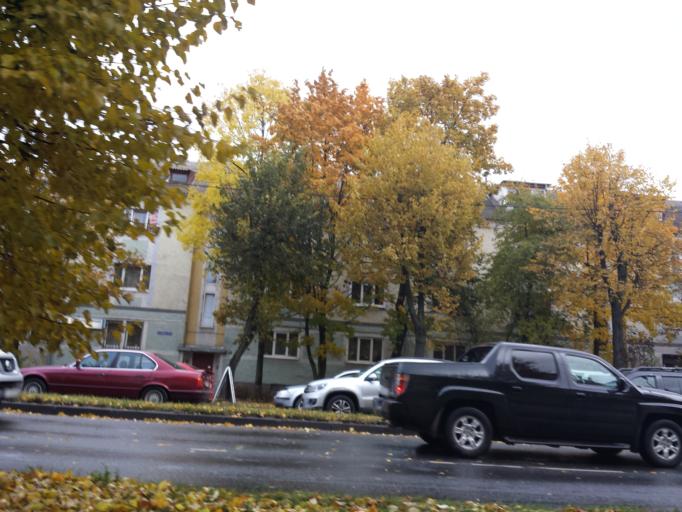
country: RU
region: Kaliningrad
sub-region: Gorod Kaliningrad
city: Kaliningrad
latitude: 54.7260
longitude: 20.5270
